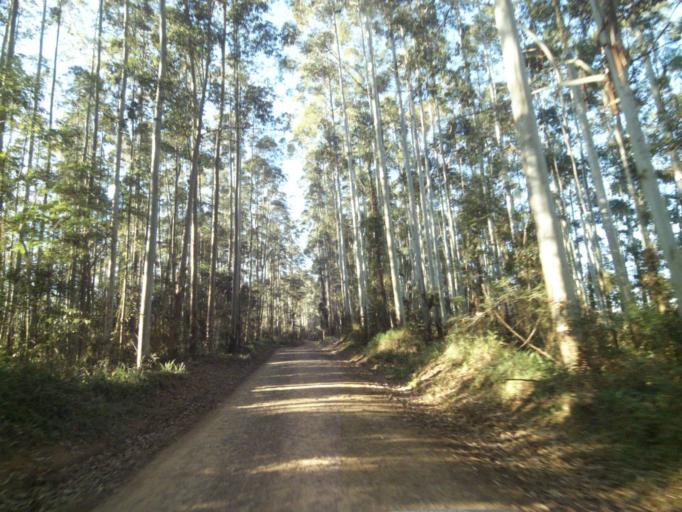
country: BR
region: Parana
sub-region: Telemaco Borba
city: Telemaco Borba
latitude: -24.5091
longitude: -50.6025
